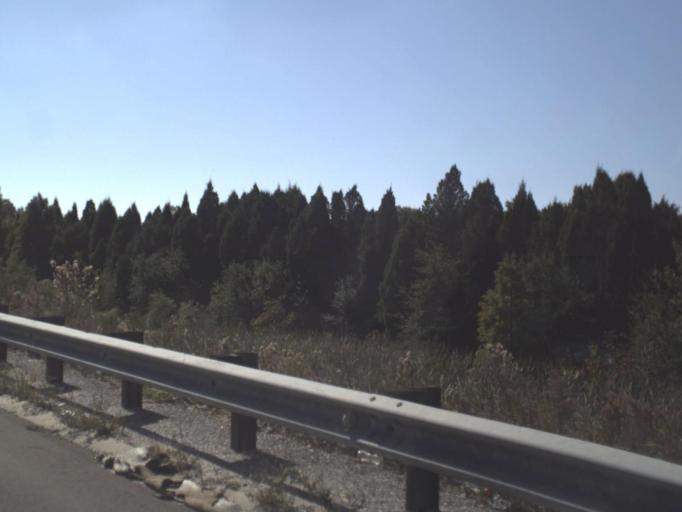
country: US
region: Florida
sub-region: Hillsborough County
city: Town 'n' Country
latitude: 28.0178
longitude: -82.5454
